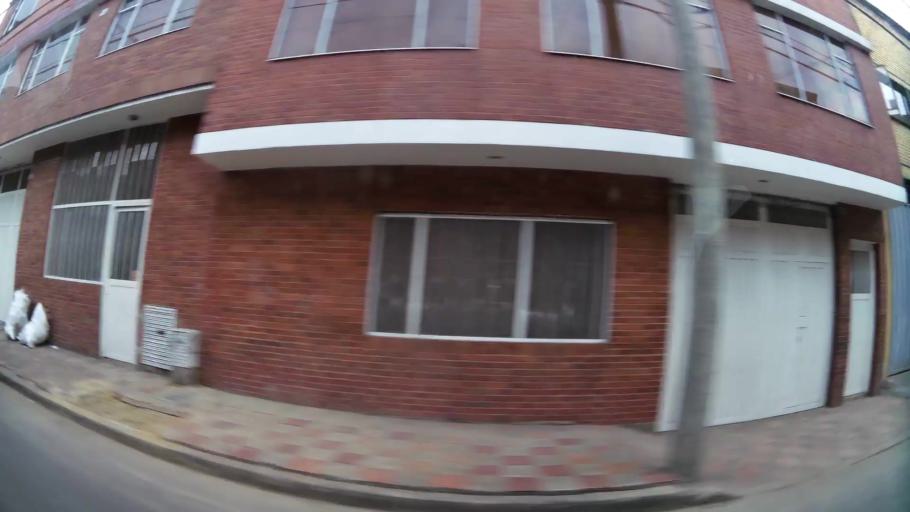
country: CO
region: Bogota D.C.
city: Bogota
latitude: 4.6051
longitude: -74.1042
